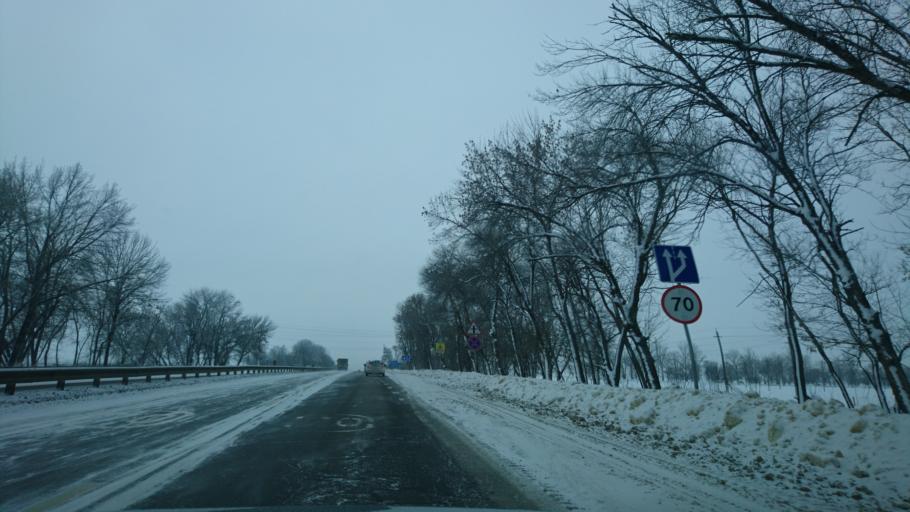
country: RU
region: Belgorod
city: Mayskiy
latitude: 50.4387
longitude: 36.3921
